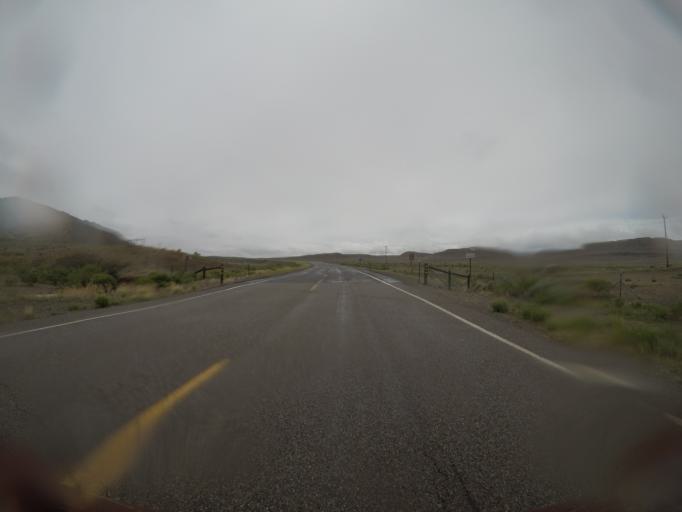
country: US
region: Wyoming
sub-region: Big Horn County
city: Lovell
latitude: 44.9505
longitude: -108.2965
